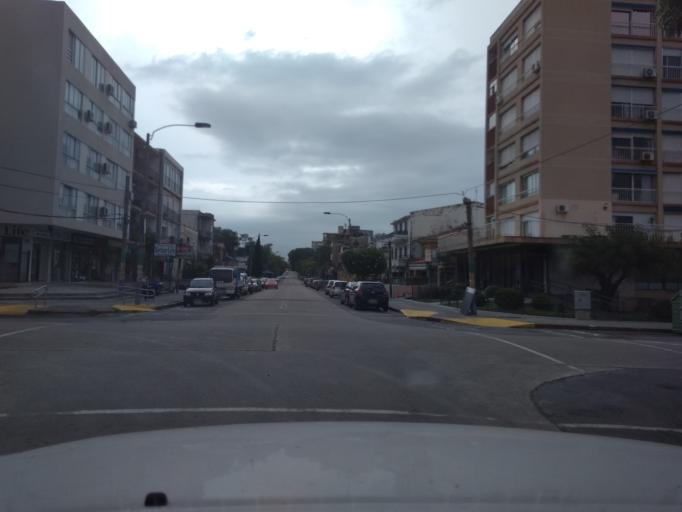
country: UY
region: Canelones
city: Paso de Carrasco
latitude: -34.8958
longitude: -56.1012
